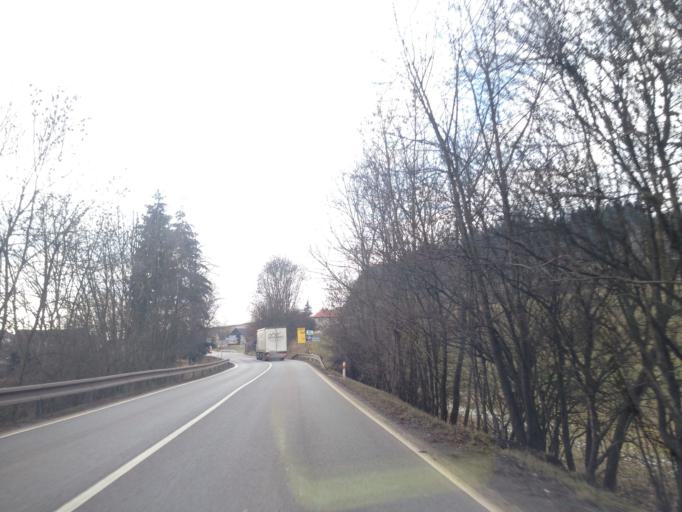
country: CZ
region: Liberecky
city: Studenec
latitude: 50.5156
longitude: 15.5602
